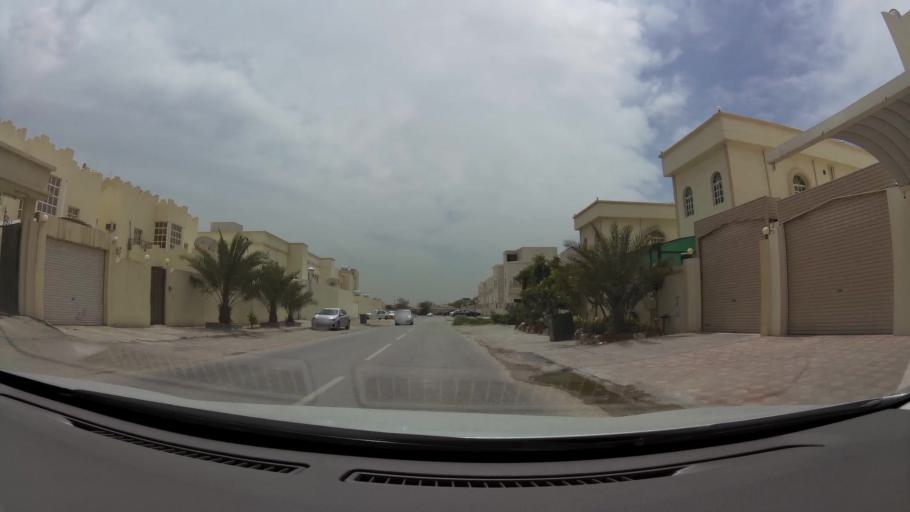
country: QA
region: Baladiyat ar Rayyan
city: Ar Rayyan
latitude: 25.2781
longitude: 51.4480
